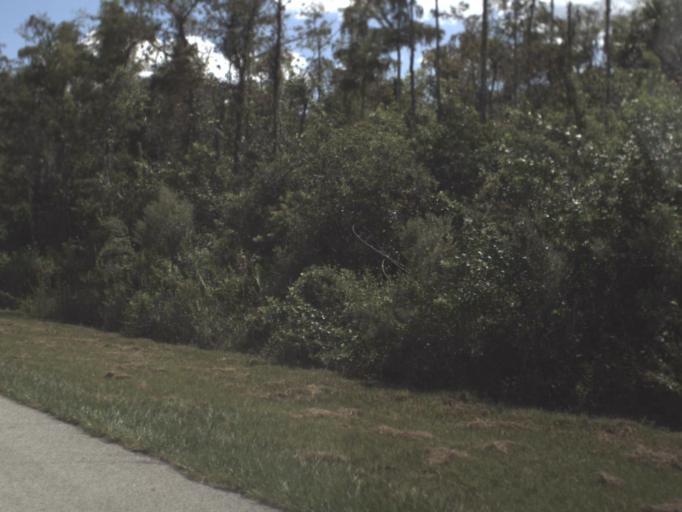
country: US
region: Florida
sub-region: Collier County
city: Lely Resort
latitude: 26.0055
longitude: -81.6090
